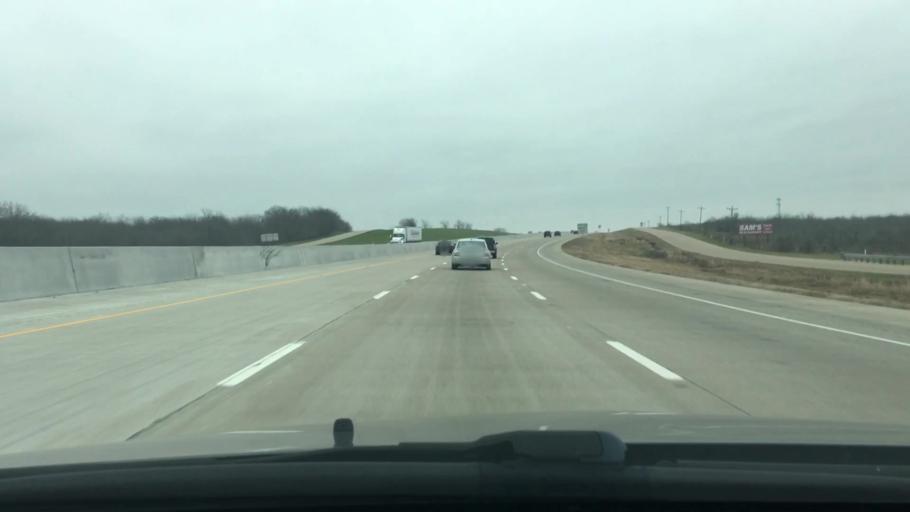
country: US
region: Texas
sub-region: Freestone County
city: Wortham
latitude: 31.8889
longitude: -96.3544
